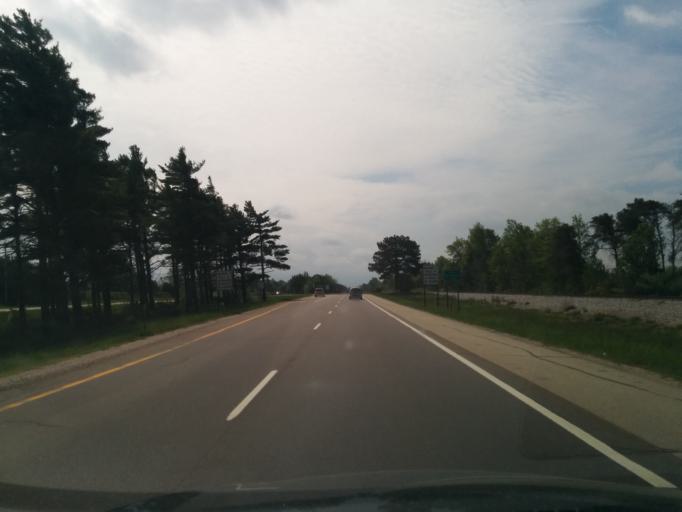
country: US
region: Michigan
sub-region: Ottawa County
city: Grand Haven
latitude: 42.9428
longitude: -86.1617
